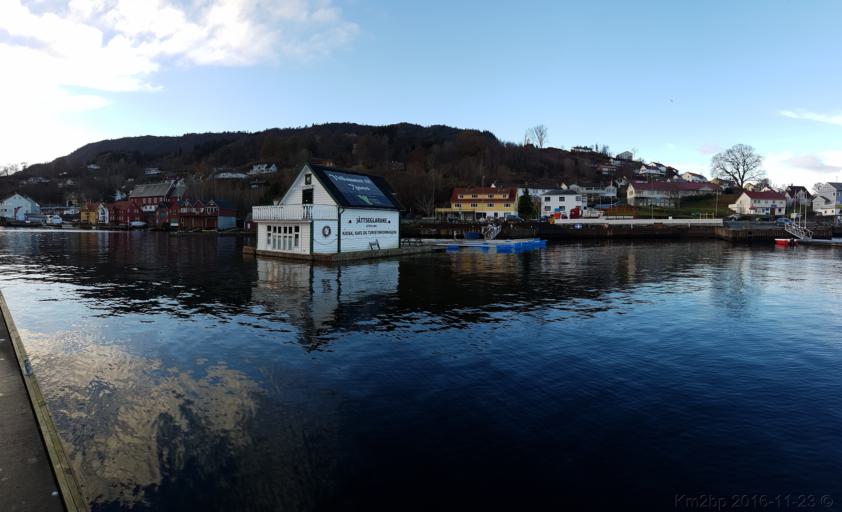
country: NO
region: Hordaland
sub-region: Tysnes
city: Uggdal
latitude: 60.0456
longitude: 5.5247
